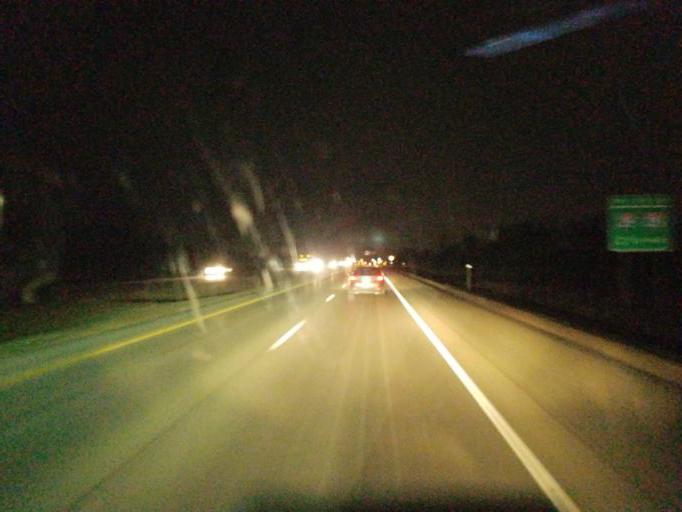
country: US
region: Iowa
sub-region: Dallas County
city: Waukee
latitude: 41.5836
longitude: -93.8254
